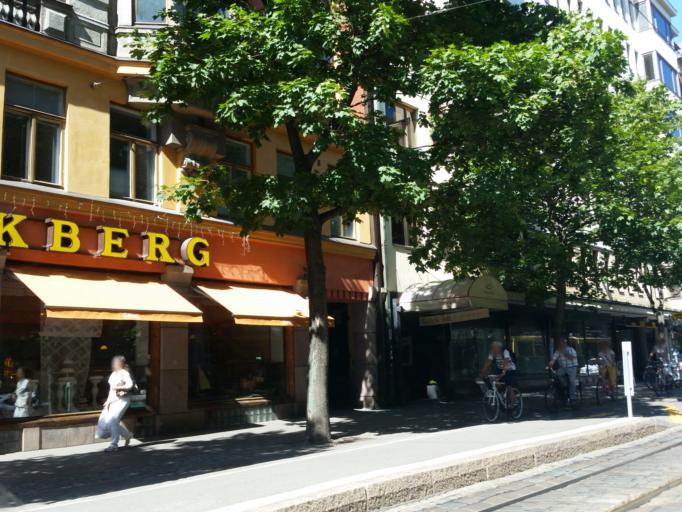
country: FI
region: Uusimaa
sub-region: Helsinki
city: Helsinki
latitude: 60.1647
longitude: 24.9378
